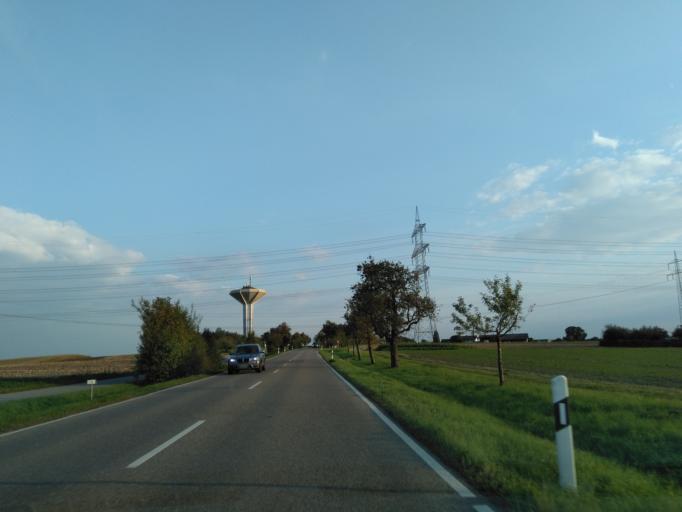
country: DE
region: Baden-Wuerttemberg
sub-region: Regierungsbezirk Stuttgart
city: Markgroningen
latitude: 48.9161
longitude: 9.0751
